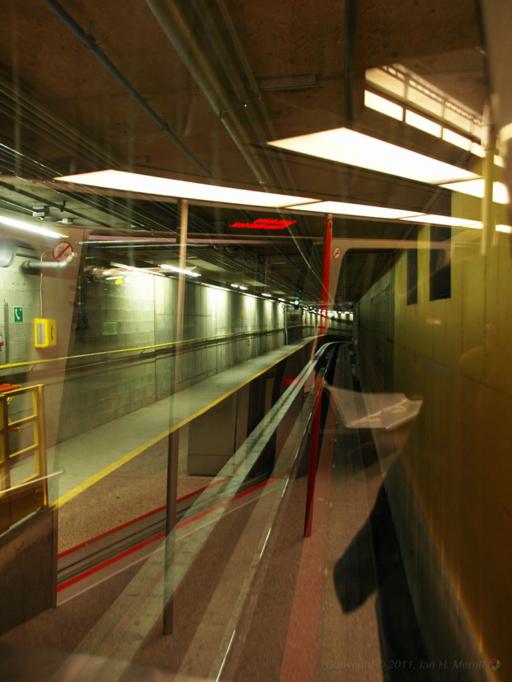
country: US
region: Washington
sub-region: King County
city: SeaTac
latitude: 47.4436
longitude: -122.3016
